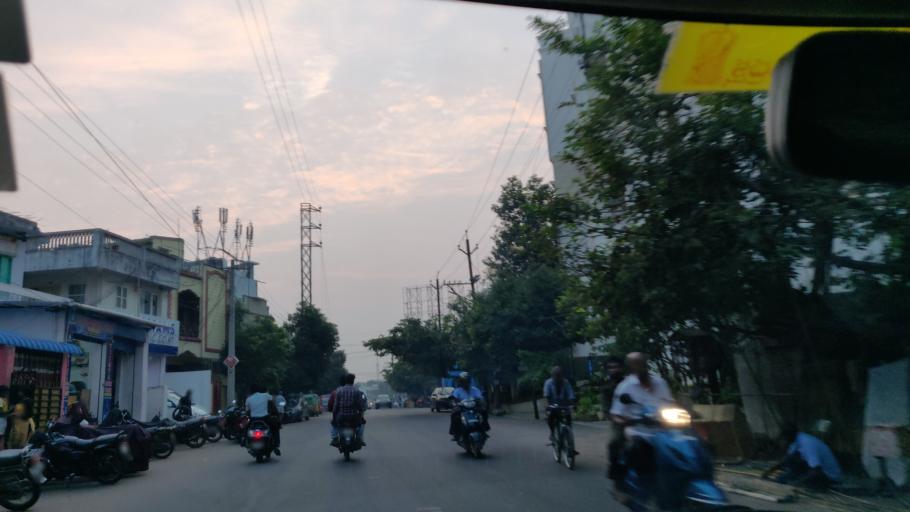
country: IN
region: Andhra Pradesh
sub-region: Krishna
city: Vijayawada
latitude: 16.5075
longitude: 80.6413
